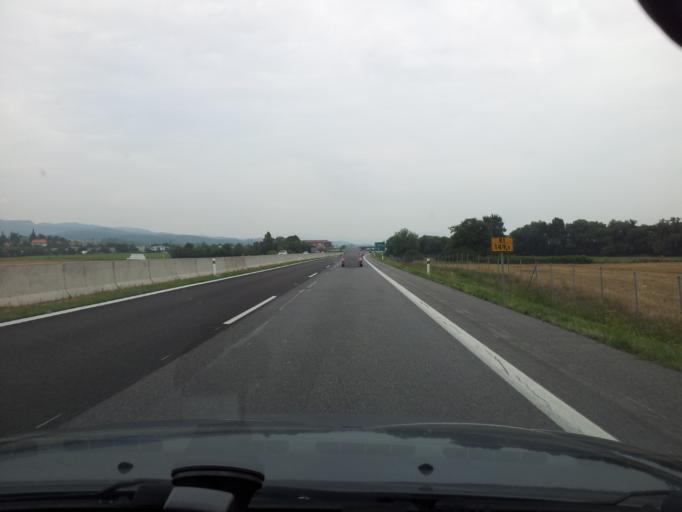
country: SK
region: Banskobystricky
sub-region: Okres Banska Bystrica
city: Zvolen
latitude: 48.6226
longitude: 19.1188
